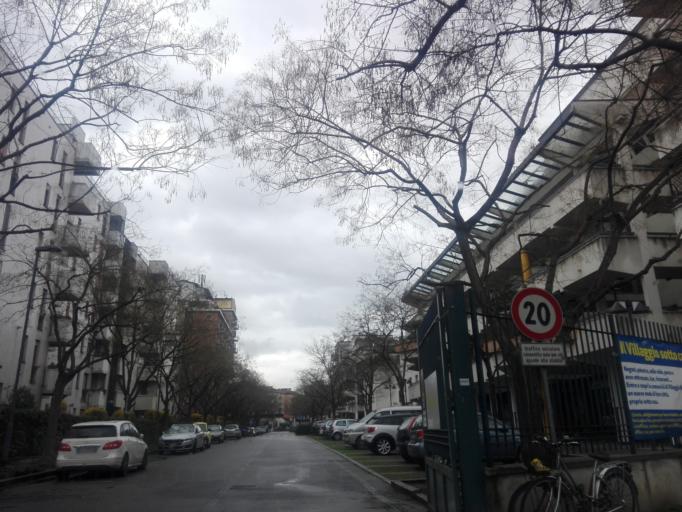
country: IT
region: Lombardy
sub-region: Citta metropolitana di Milano
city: Romano Banco
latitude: 45.4410
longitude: 9.1572
